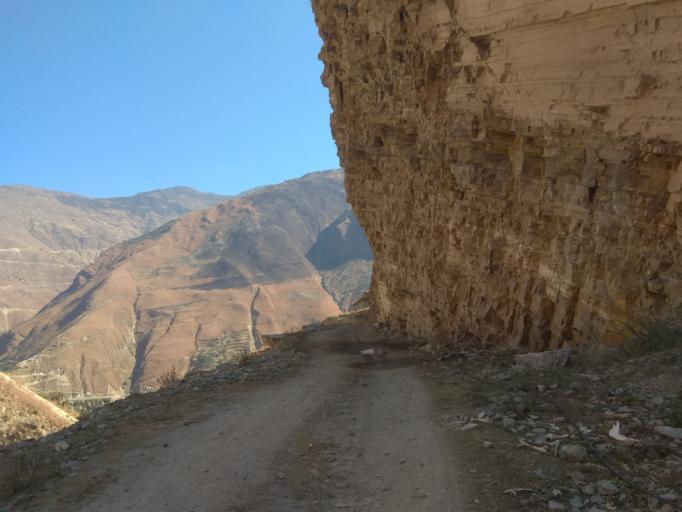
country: NP
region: Mid Western
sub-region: Karnali Zone
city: Jumla
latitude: 29.2990
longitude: 81.7422
